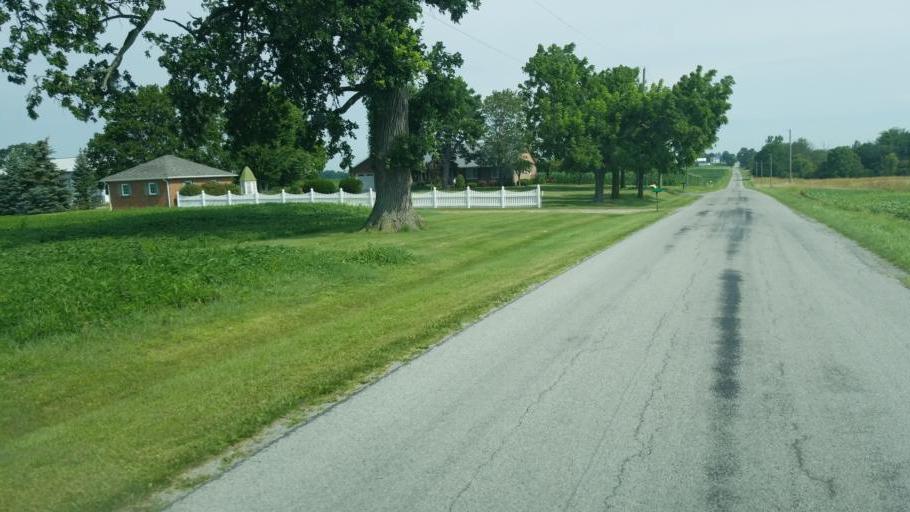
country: US
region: Ohio
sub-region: Wyandot County
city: Upper Sandusky
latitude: 40.7761
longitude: -83.3237
